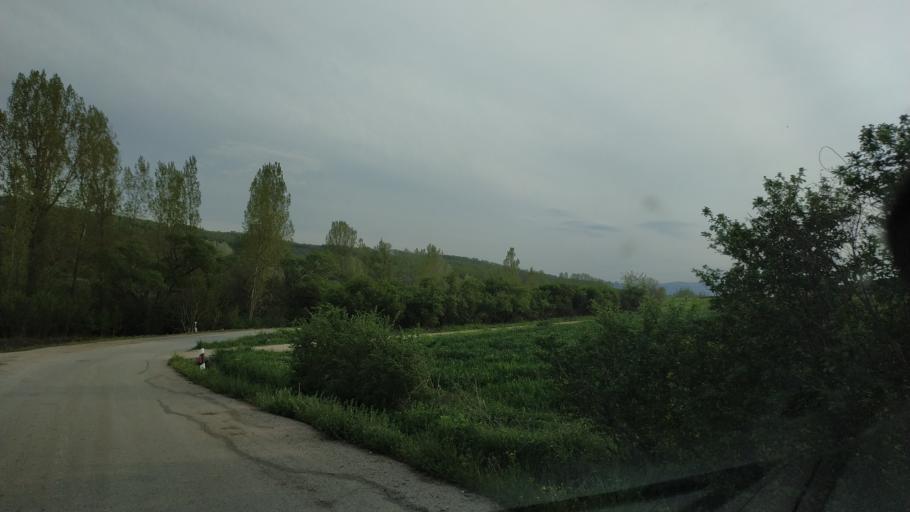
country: RS
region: Central Serbia
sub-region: Nisavski Okrug
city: Aleksinac
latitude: 43.5057
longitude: 21.8415
